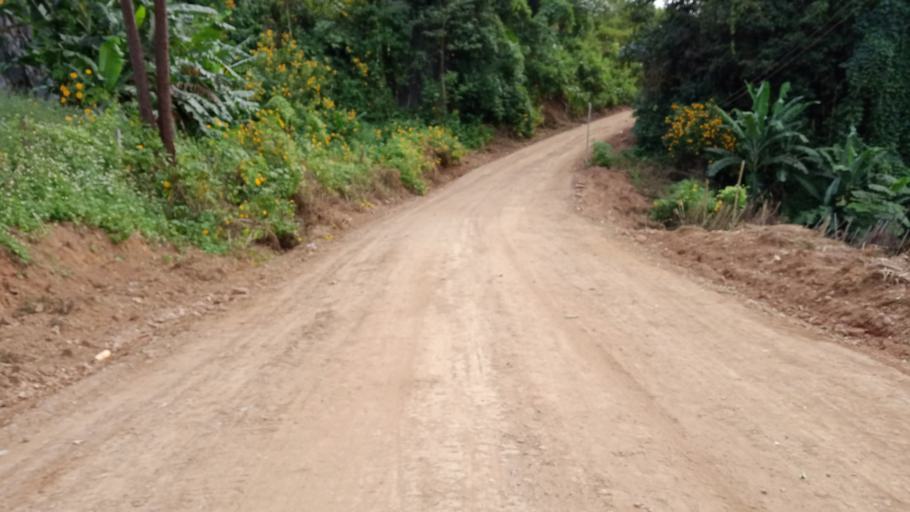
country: LA
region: Xiangkhoang
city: Phonsavan
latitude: 19.1186
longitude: 102.9125
